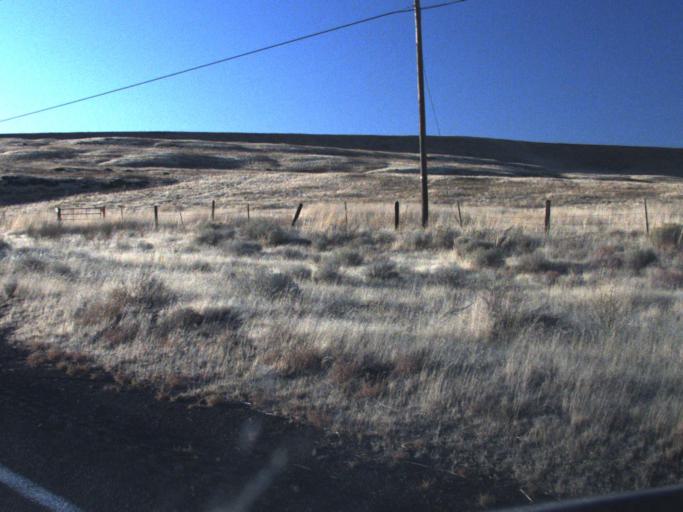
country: US
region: Washington
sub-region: Franklin County
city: Connell
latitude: 46.6509
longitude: -118.5206
